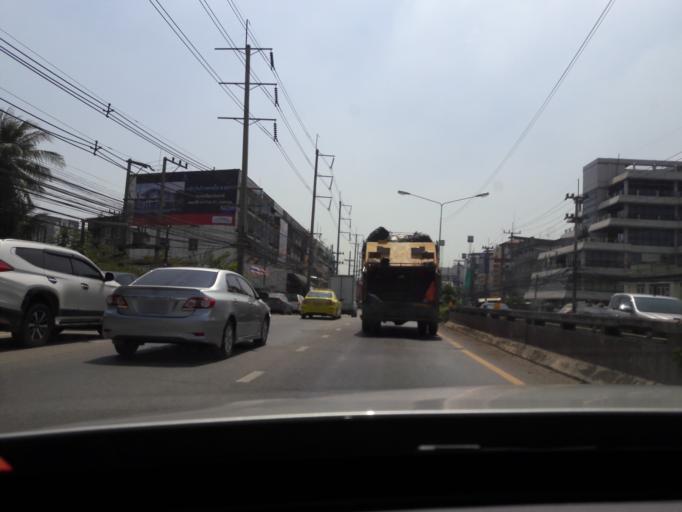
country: TH
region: Samut Sakhon
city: Samut Sakhon
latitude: 13.5701
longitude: 100.2721
